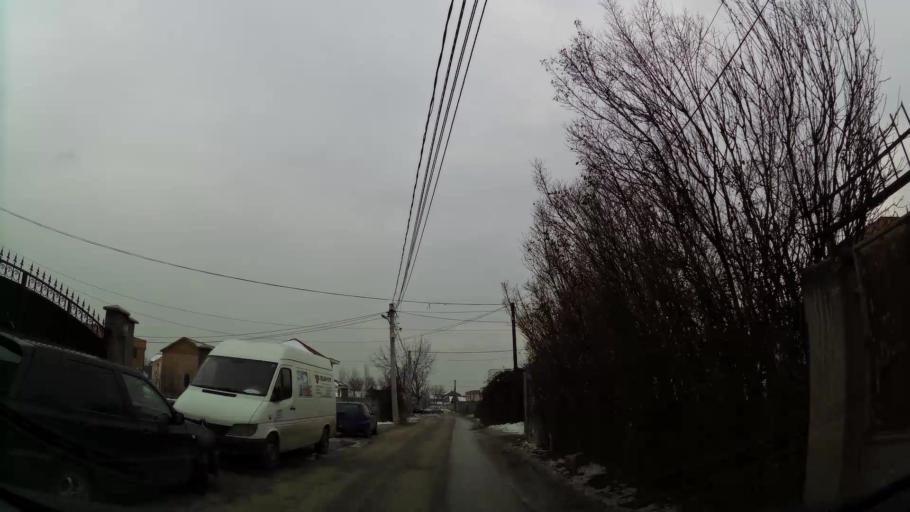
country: MK
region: Suto Orizari
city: Suto Orizare
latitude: 42.0329
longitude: 21.4231
